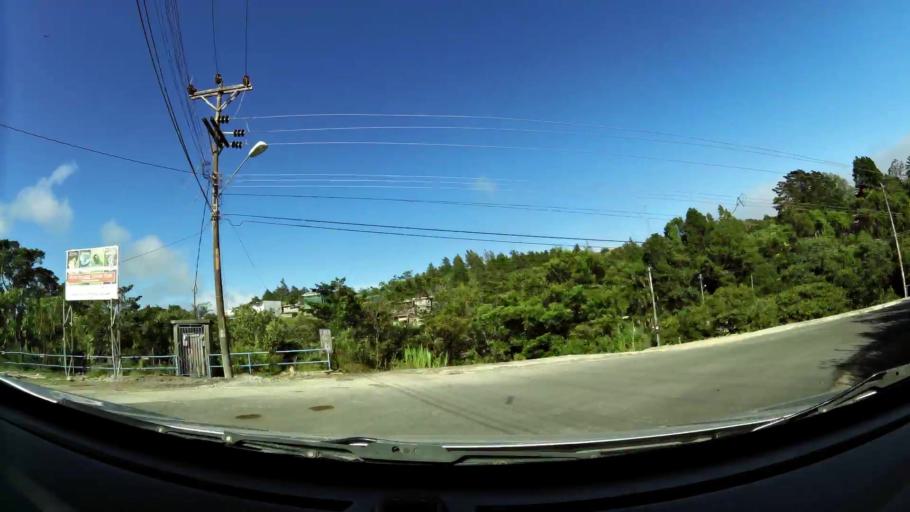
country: CR
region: Guanacaste
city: Juntas
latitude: 10.3154
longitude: -84.8246
